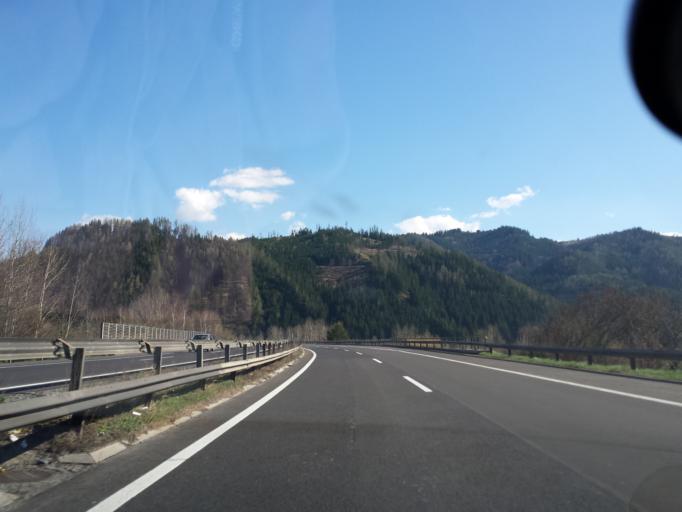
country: AT
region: Styria
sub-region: Politischer Bezirk Leoben
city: Sankt Michael in Obersteiermark
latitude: 47.3394
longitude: 15.0076
